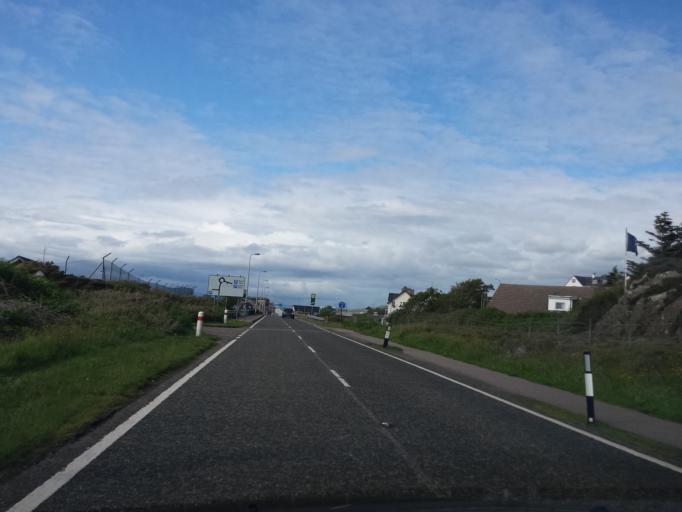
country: GB
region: Scotland
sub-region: Highland
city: Portree
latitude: 57.0026
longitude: -5.8327
